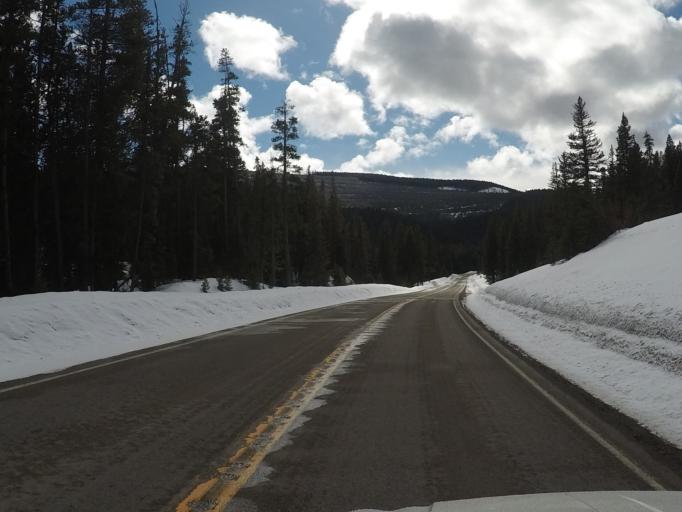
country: US
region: Montana
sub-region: Meagher County
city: White Sulphur Springs
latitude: 46.7630
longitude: -110.7140
